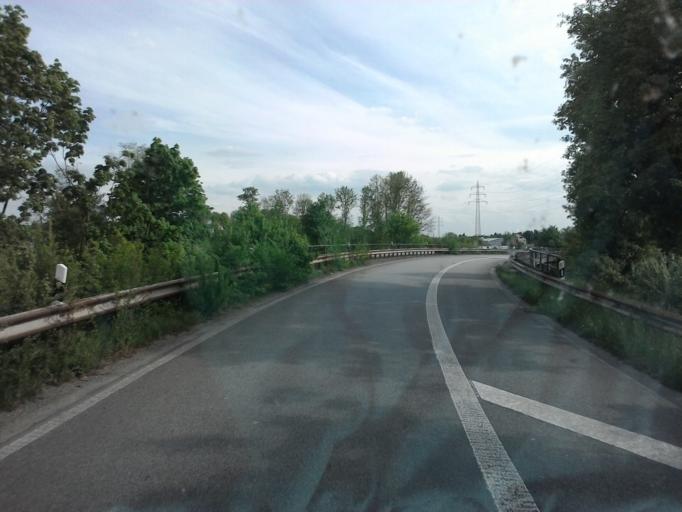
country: DE
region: North Rhine-Westphalia
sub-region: Regierungsbezirk Dusseldorf
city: Moers
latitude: 51.4393
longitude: 6.6702
